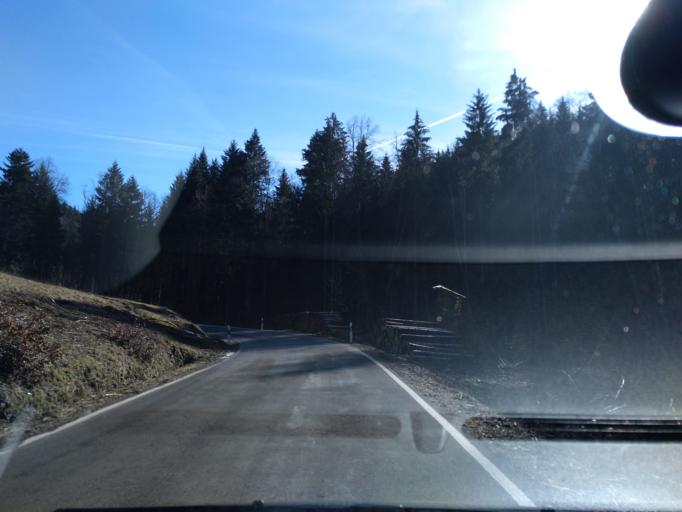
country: DE
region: Baden-Wuerttemberg
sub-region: Regierungsbezirk Stuttgart
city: Mainhardt
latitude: 49.0977
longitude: 9.5391
